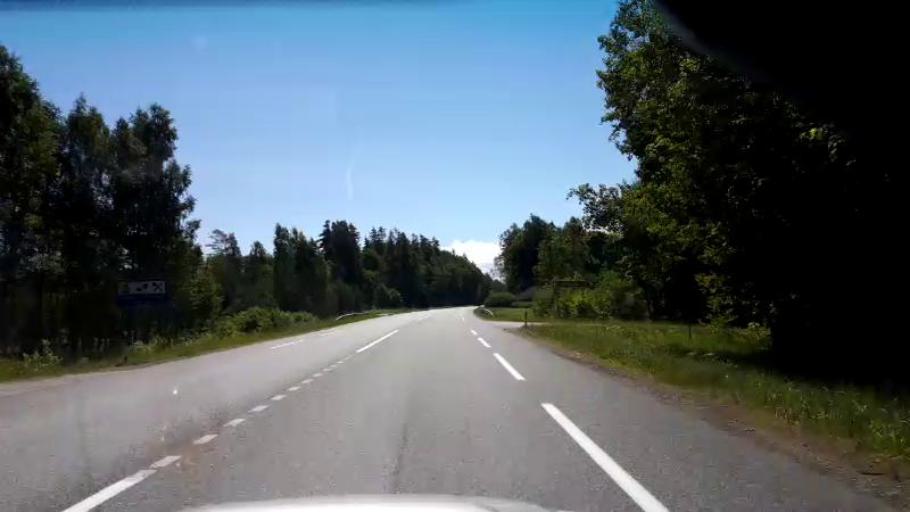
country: LV
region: Saulkrastu
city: Saulkrasti
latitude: 57.3669
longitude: 24.4368
